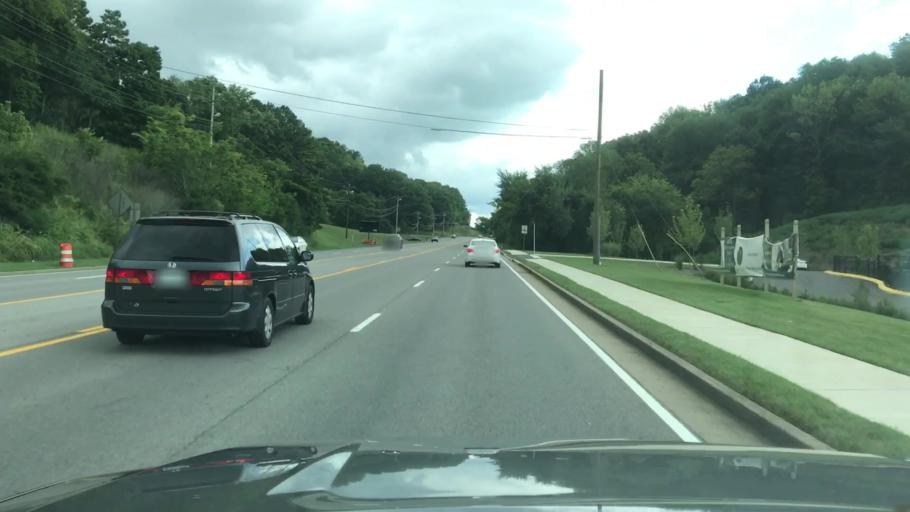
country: US
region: Tennessee
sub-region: Williamson County
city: Franklin
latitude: 35.9730
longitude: -86.8302
